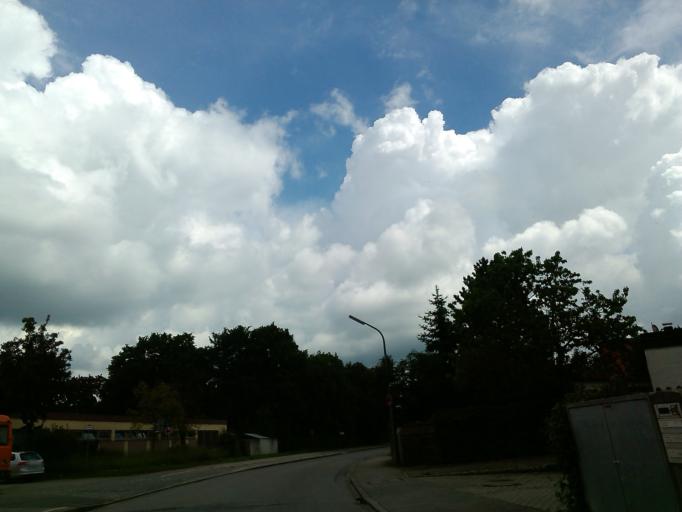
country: DE
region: Bavaria
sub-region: Upper Bavaria
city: Neubiberg
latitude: 48.1131
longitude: 11.6665
